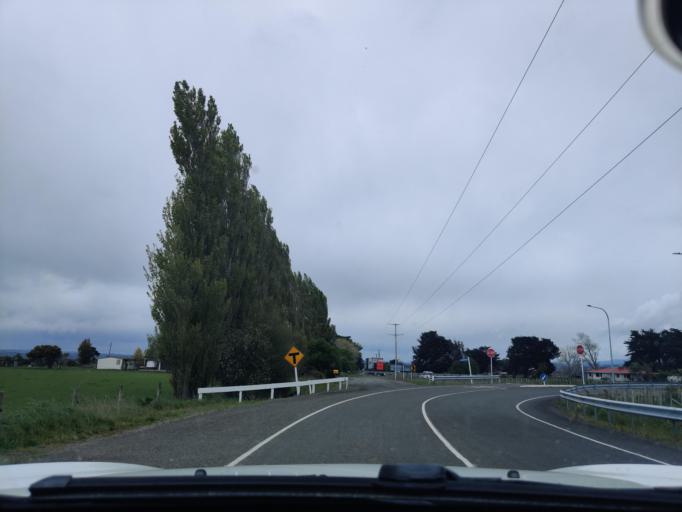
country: NZ
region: Manawatu-Wanganui
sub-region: Palmerston North City
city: Palmerston North
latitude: -40.3182
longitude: 175.8561
